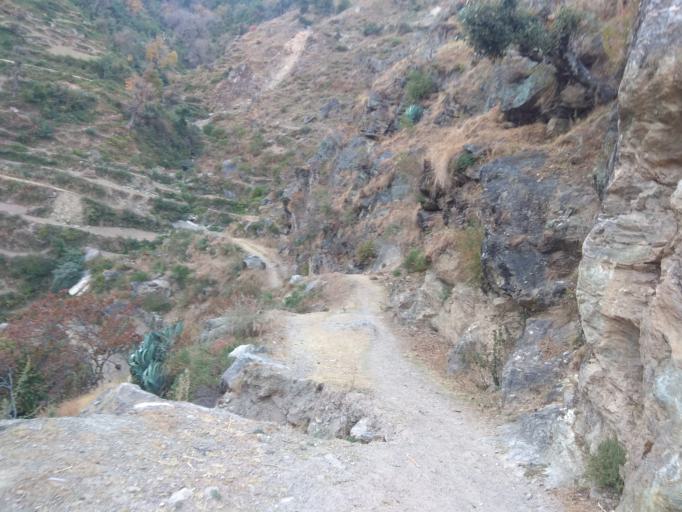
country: NP
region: Mid Western
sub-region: Karnali Zone
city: Jumla
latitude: 29.3238
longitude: 81.7187
